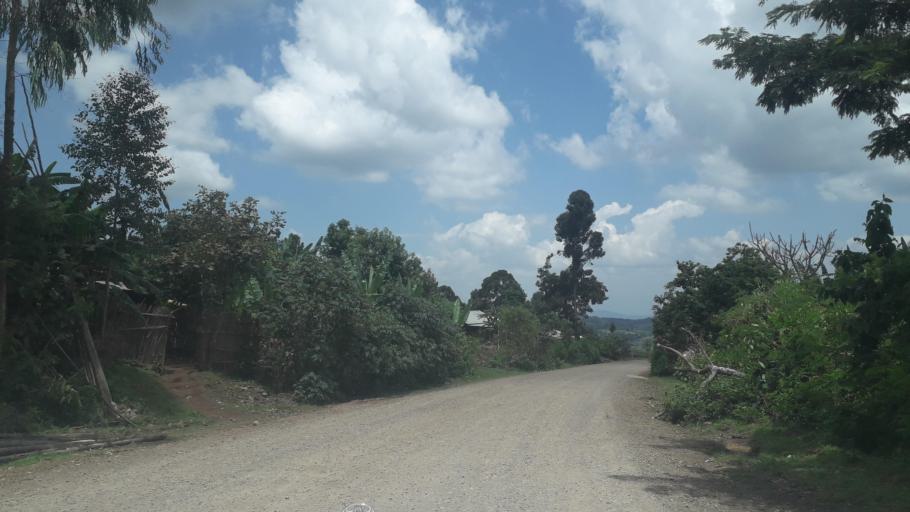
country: ET
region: Oromiya
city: Jima
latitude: 7.4651
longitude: 36.8745
